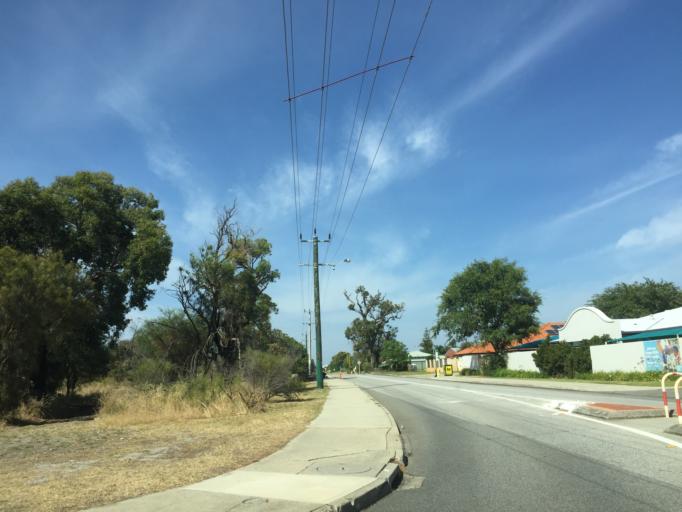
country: AU
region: Western Australia
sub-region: Gosnells
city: Thornlie
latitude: -32.0816
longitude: 115.9611
